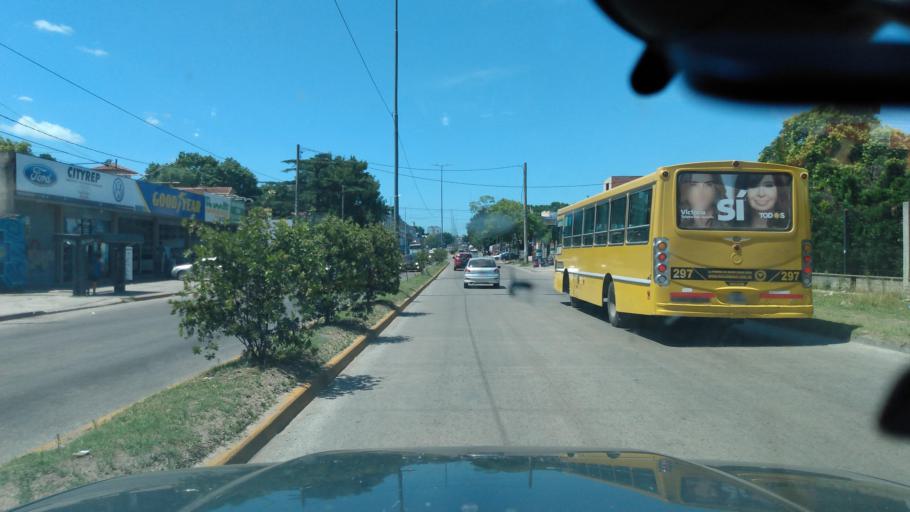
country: AR
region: Buenos Aires
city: Hurlingham
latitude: -34.5557
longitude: -58.7262
